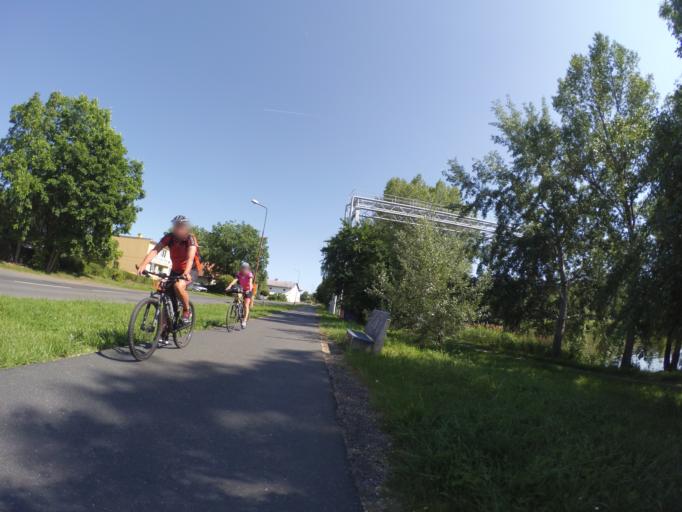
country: CZ
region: Central Bohemia
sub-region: Okres Nymburk
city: Podebrady
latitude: 50.1584
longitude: 15.1052
